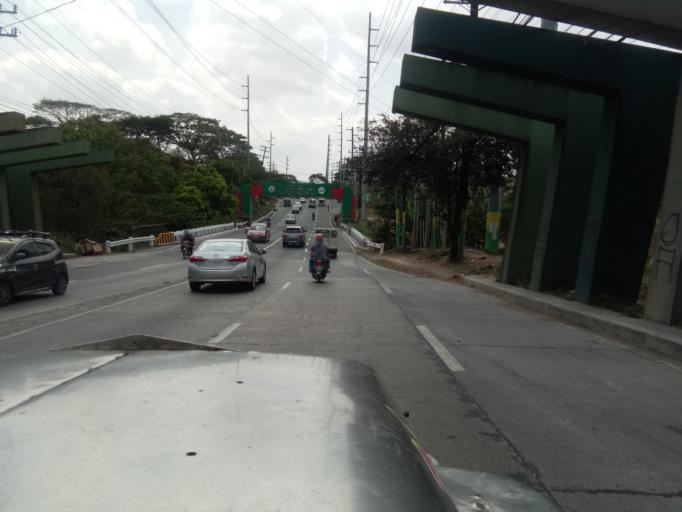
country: PH
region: Calabarzon
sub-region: Province of Cavite
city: Manggahan
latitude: 14.2916
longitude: 120.9298
